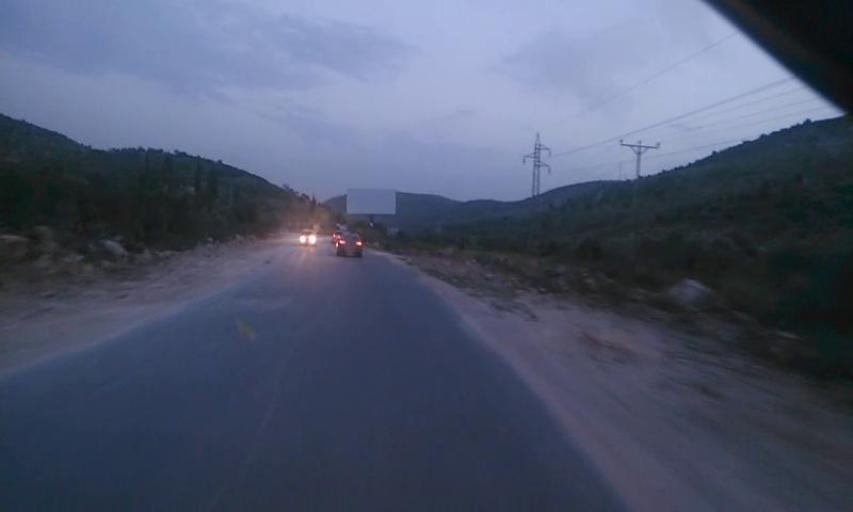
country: PS
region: West Bank
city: `Anabta
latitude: 32.2967
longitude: 35.1321
